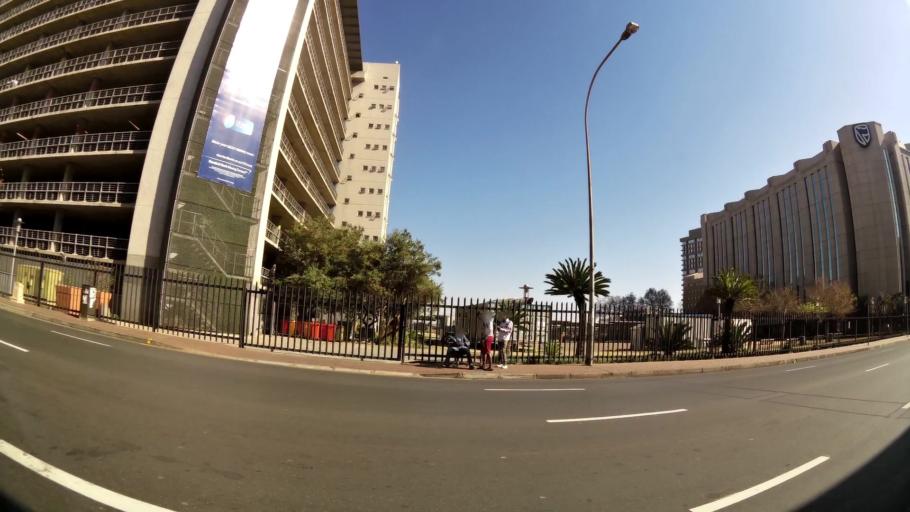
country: ZA
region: Gauteng
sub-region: City of Johannesburg Metropolitan Municipality
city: Johannesburg
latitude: -26.2111
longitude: 28.0397
